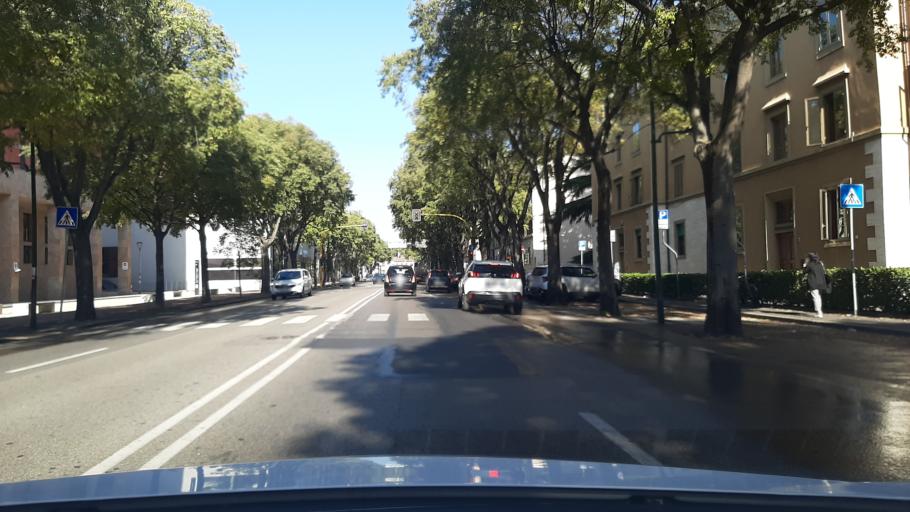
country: IT
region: Tuscany
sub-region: Province of Florence
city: Florence
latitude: 43.7916
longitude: 11.2309
